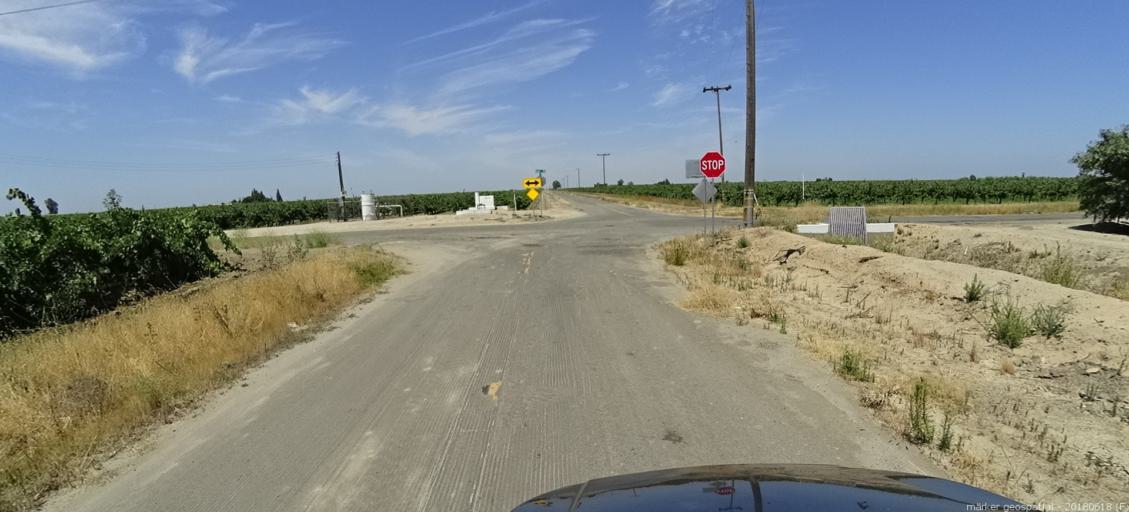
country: US
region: California
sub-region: Madera County
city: Parkwood
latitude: 36.8948
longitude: -120.1102
